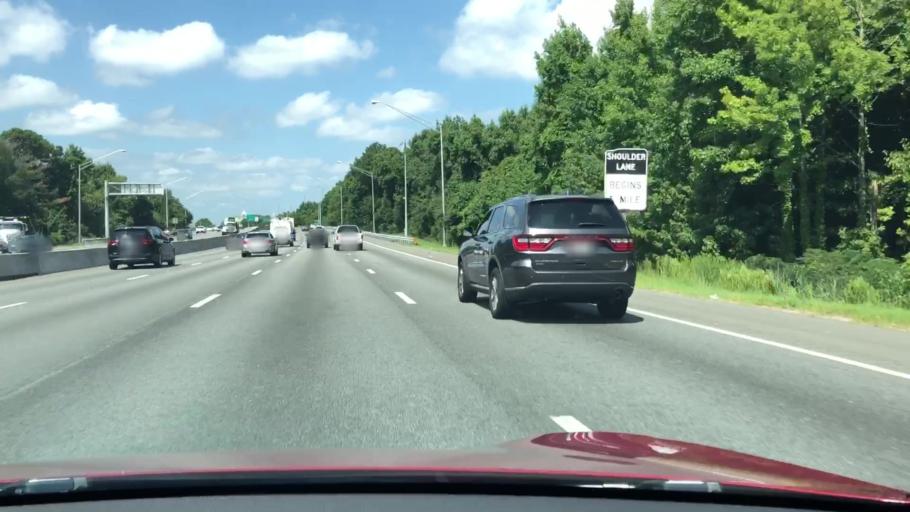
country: US
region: Virginia
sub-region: City of Virginia Beach
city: Virginia Beach
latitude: 36.8393
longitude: -76.0857
